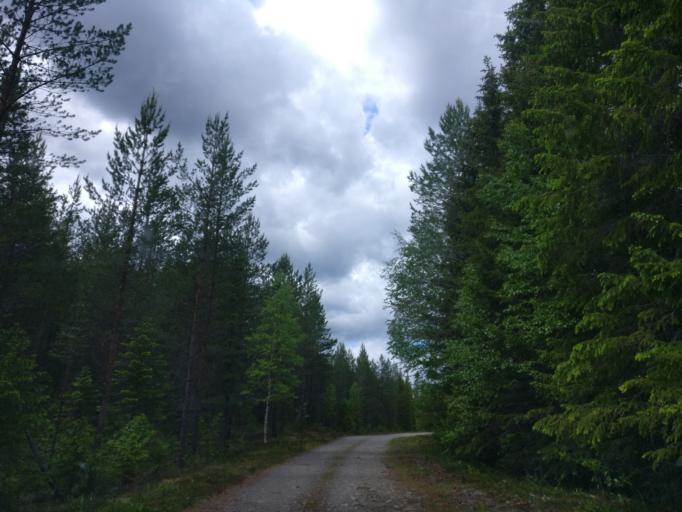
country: SE
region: Jaemtland
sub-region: Harjedalens Kommun
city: Sveg
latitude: 62.1953
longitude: 13.4148
